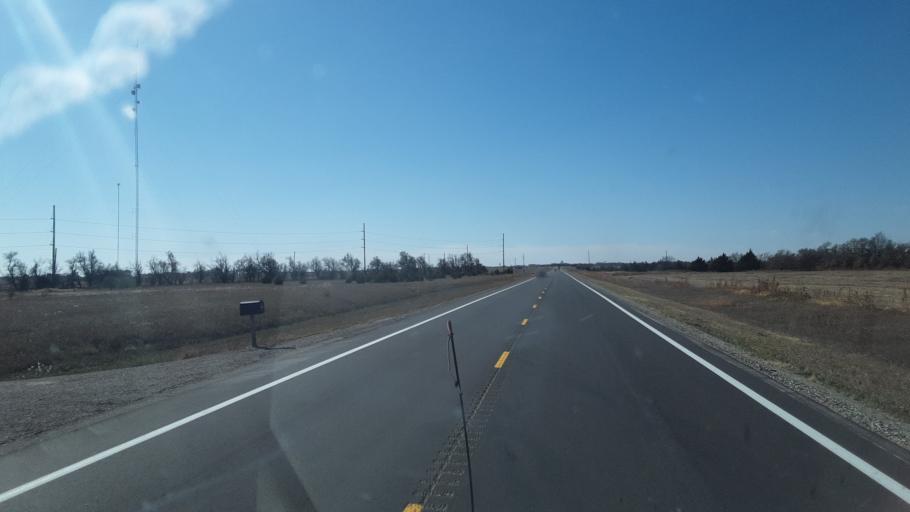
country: US
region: Kansas
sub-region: Rice County
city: Lyons
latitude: 38.3708
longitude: -98.1420
